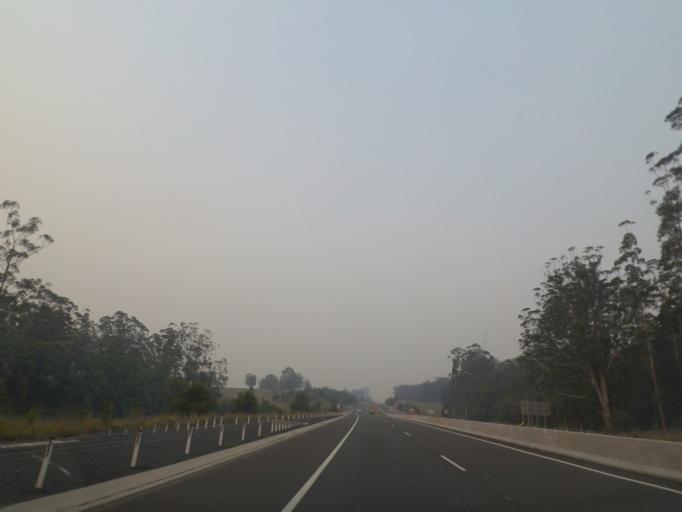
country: AU
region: New South Wales
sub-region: Nambucca Shire
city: Macksville
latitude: -30.7799
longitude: 152.8927
